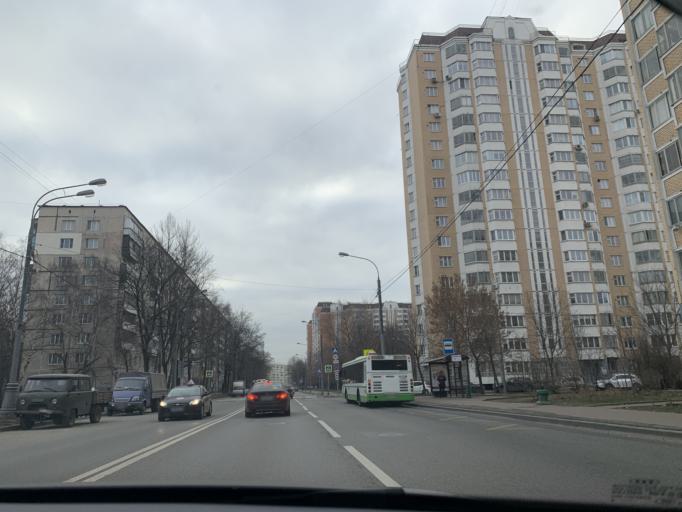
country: RU
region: Moskovskaya
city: Vostochnoe Degunino
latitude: 55.8674
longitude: 37.5634
